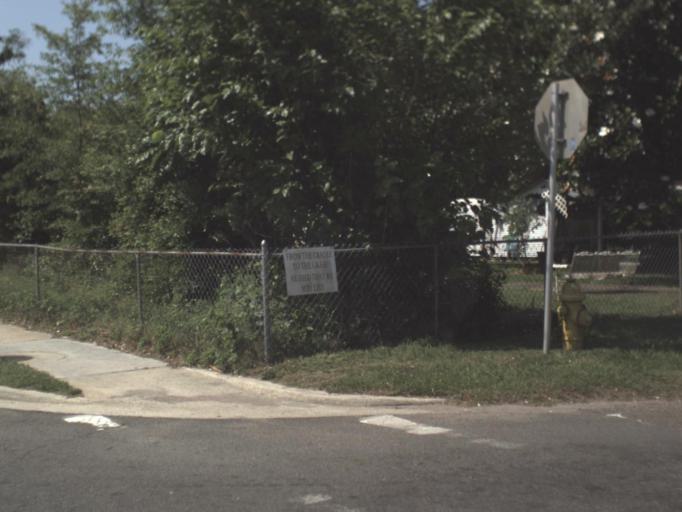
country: US
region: Florida
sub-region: Duval County
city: Jacksonville
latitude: 30.4047
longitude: -81.6857
